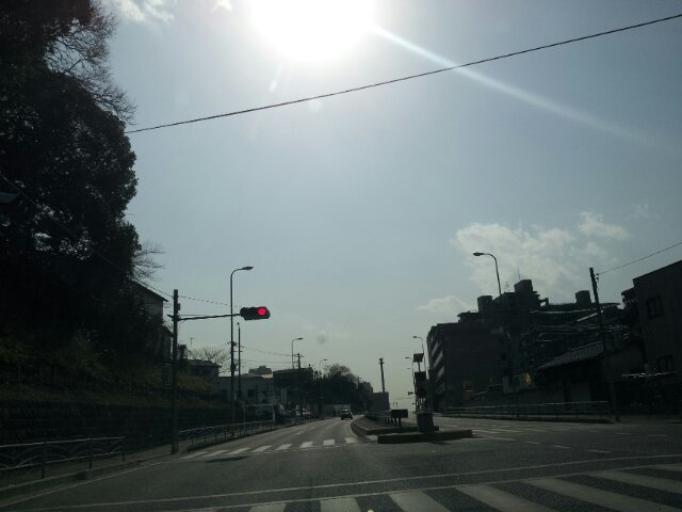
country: JP
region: Kanagawa
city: Yokohama
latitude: 35.4959
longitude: 139.6598
